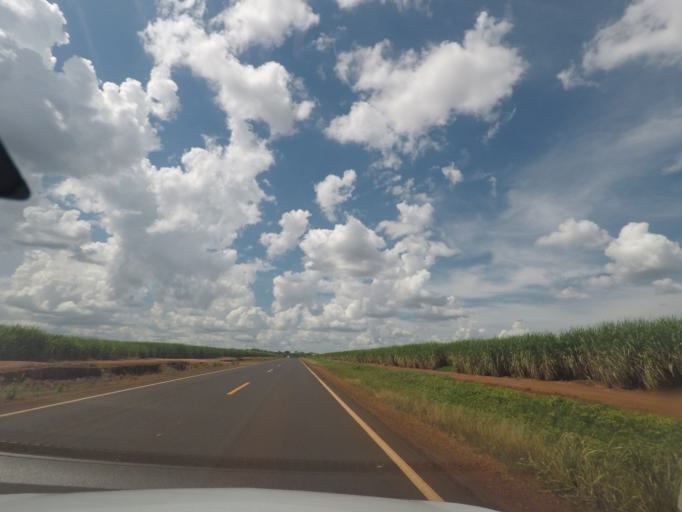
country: BR
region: Minas Gerais
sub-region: Conceicao Das Alagoas
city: Conceicao das Alagoas
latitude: -19.8555
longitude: -48.5996
